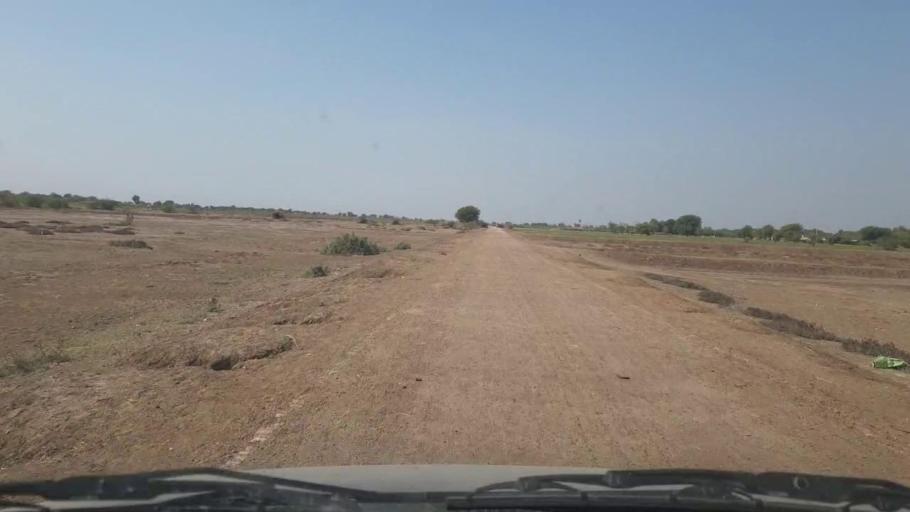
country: PK
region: Sindh
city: Samaro
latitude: 25.2400
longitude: 69.3334
